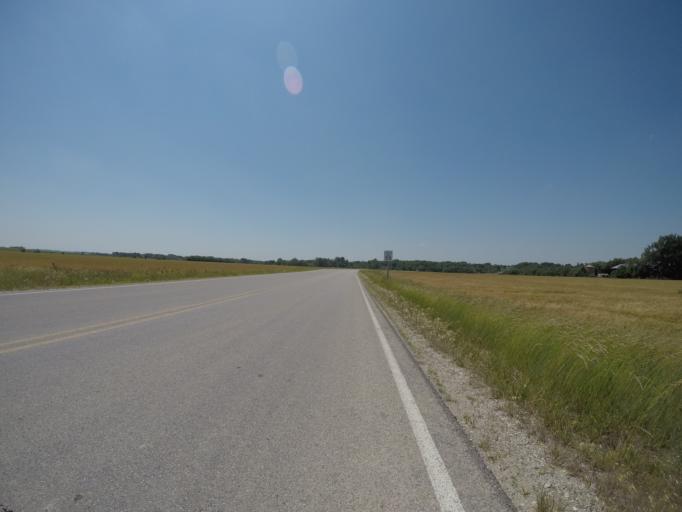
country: US
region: Kansas
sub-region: Pottawatomie County
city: Westmoreland
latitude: 39.2905
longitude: -96.4406
